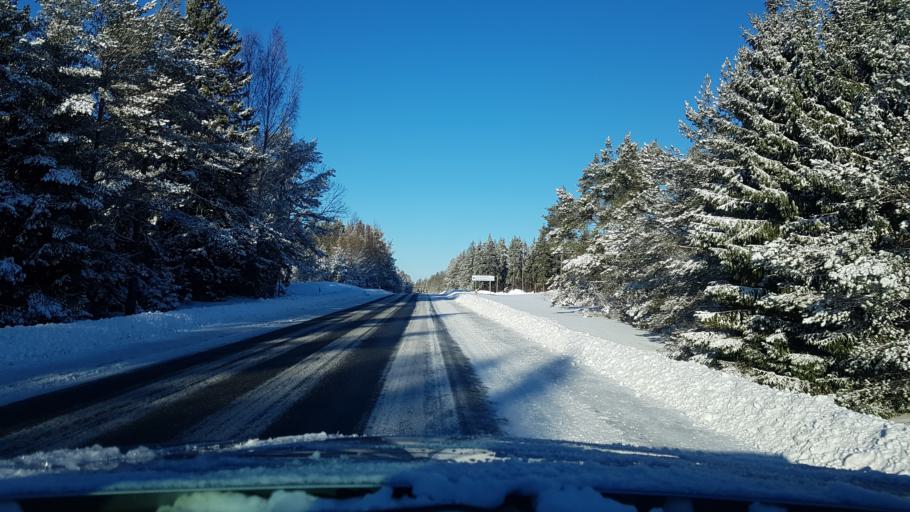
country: EE
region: Hiiumaa
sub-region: Kaerdla linn
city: Kardla
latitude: 58.9702
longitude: 22.8271
